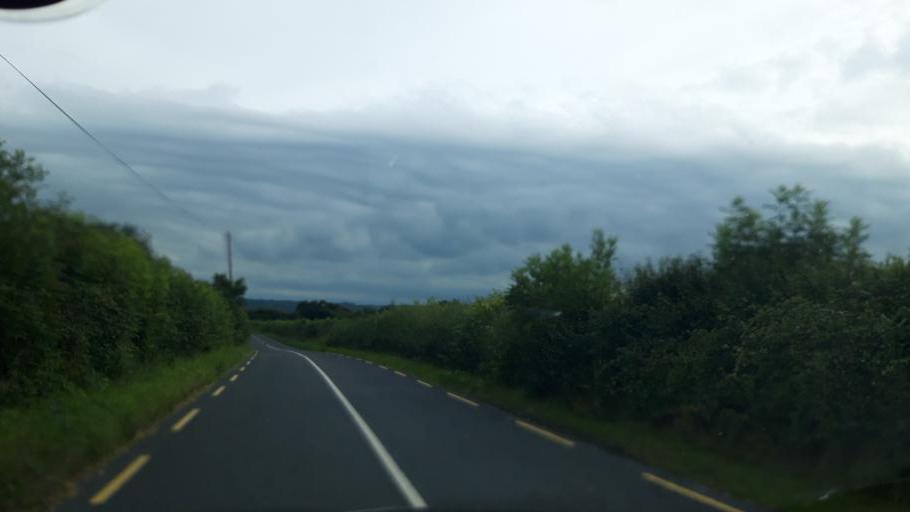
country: IE
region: Leinster
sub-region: Kilkenny
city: Ballyragget
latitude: 52.7539
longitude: -7.3920
